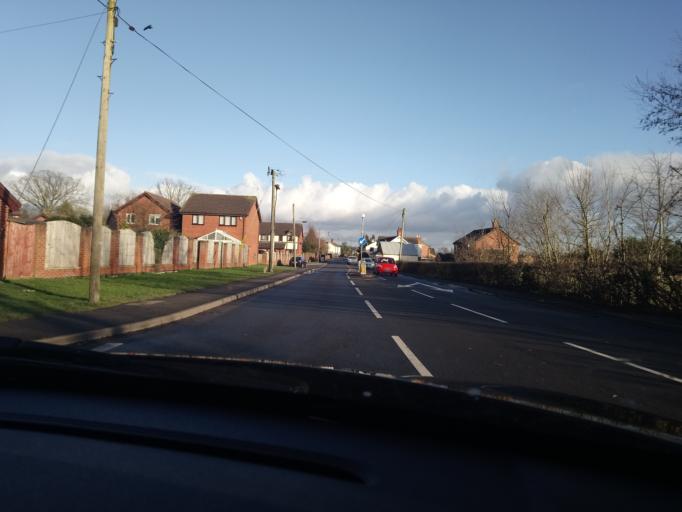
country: GB
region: Wales
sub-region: Wrexham
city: Overton
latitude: 52.9245
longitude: -2.9394
